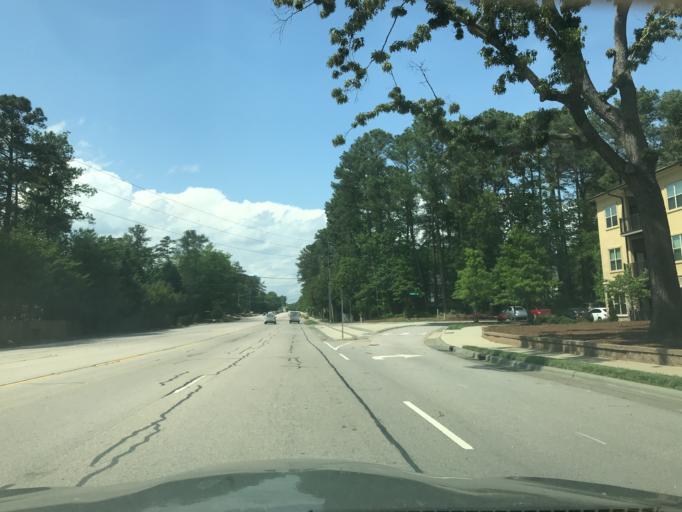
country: US
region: North Carolina
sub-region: Wake County
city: West Raleigh
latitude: 35.8902
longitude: -78.6478
